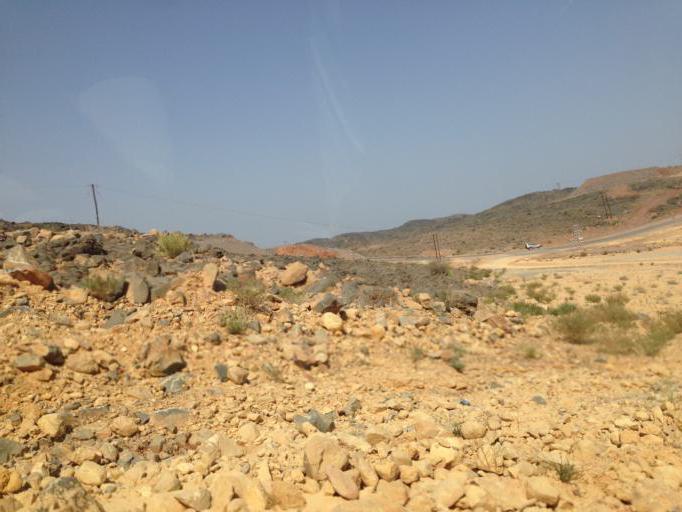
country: OM
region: Ash Sharqiyah
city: Ibra'
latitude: 23.0870
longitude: 58.9489
